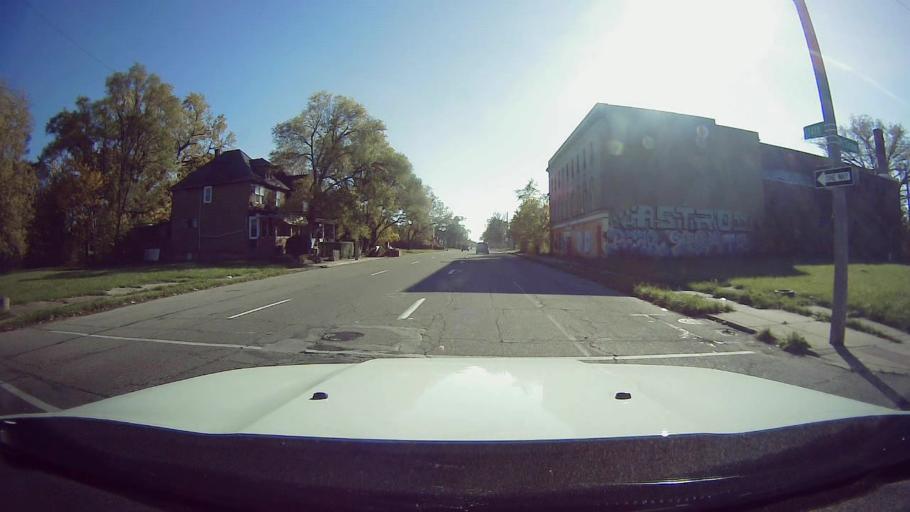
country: US
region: Michigan
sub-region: Wayne County
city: Highland Park
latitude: 42.3580
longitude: -83.0917
